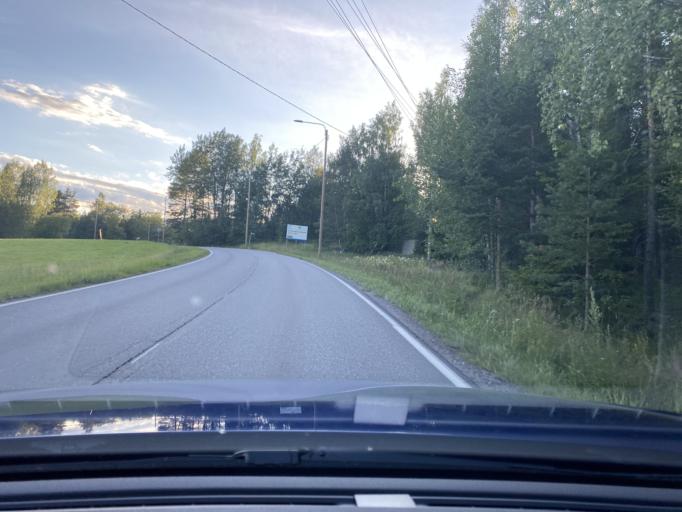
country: FI
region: Uusimaa
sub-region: Helsinki
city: Nurmijaervi
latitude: 60.4103
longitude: 24.7723
